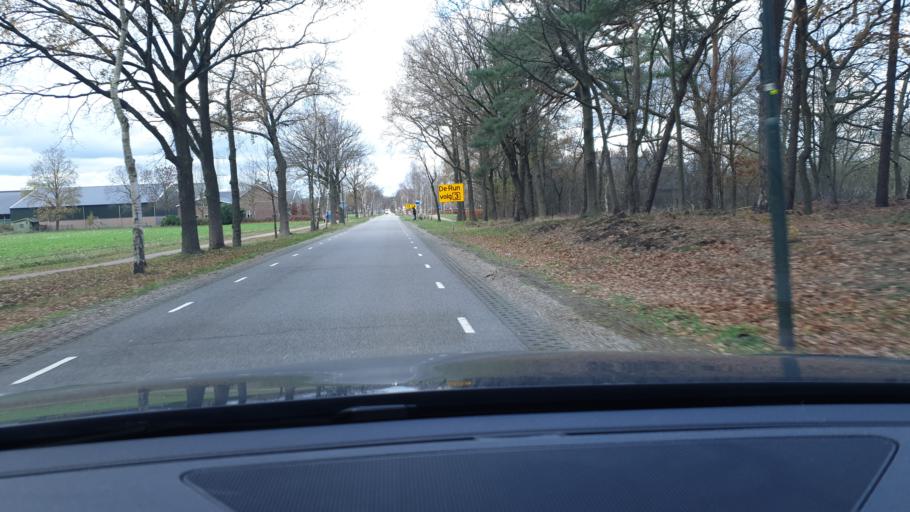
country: NL
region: North Brabant
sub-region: Gemeente Veldhoven
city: Veldhoven
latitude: 51.3875
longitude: 5.4100
